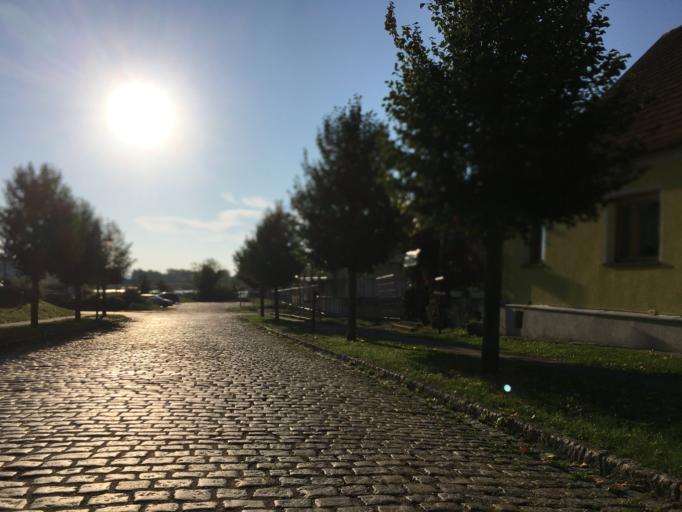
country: DE
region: Brandenburg
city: Lebus
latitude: 52.4253
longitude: 14.5409
